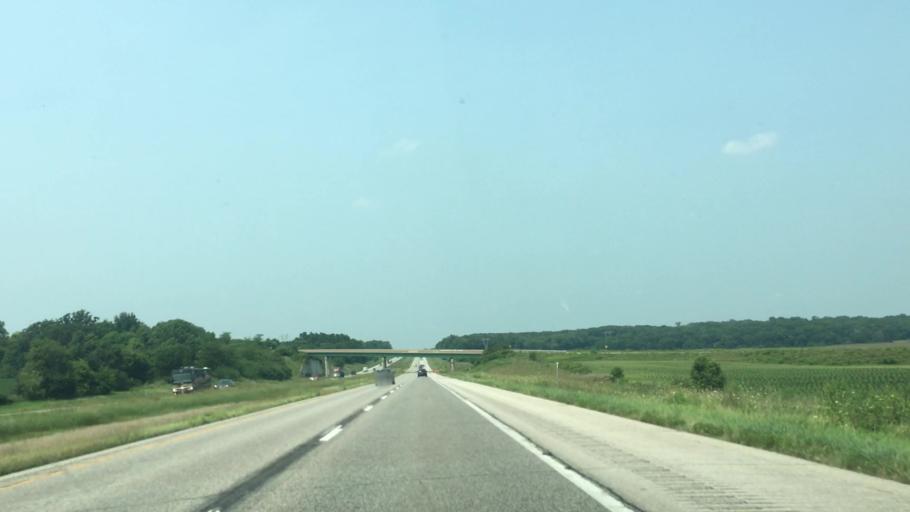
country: US
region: Iowa
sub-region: Linn County
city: Center Point
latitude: 42.2010
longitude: -91.8287
